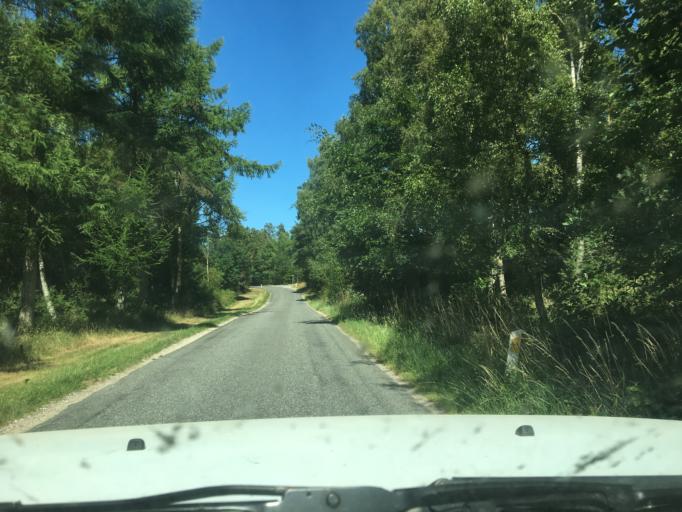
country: DK
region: Central Jutland
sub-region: Syddjurs Kommune
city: Ryomgard
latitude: 56.4840
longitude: 10.5941
